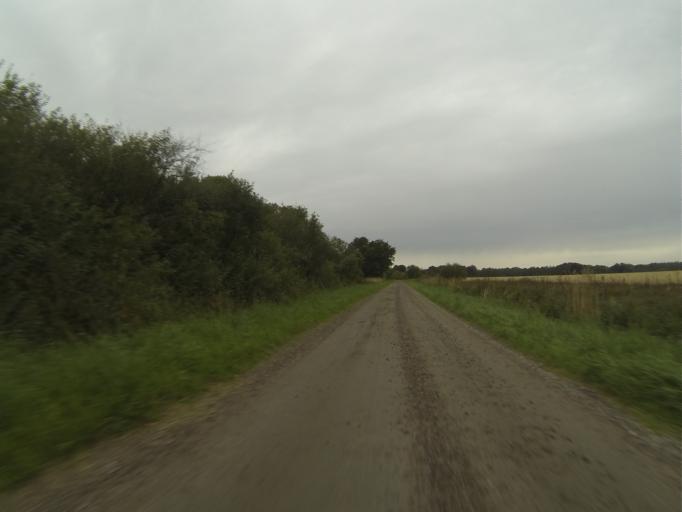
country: SE
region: Skane
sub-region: Lunds Kommun
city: Veberod
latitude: 55.7136
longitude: 13.4169
